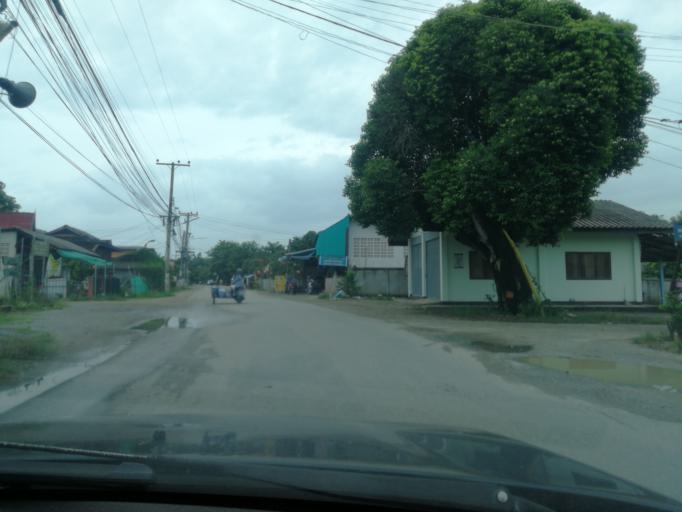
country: TH
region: Chiang Mai
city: San Pa Tong
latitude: 18.6000
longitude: 98.9103
